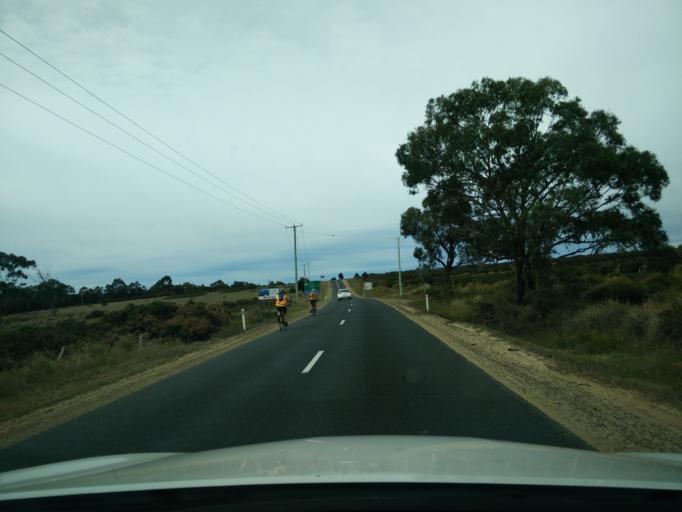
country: AU
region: Tasmania
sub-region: Break O'Day
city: St Helens
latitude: -41.9365
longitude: 148.2228
